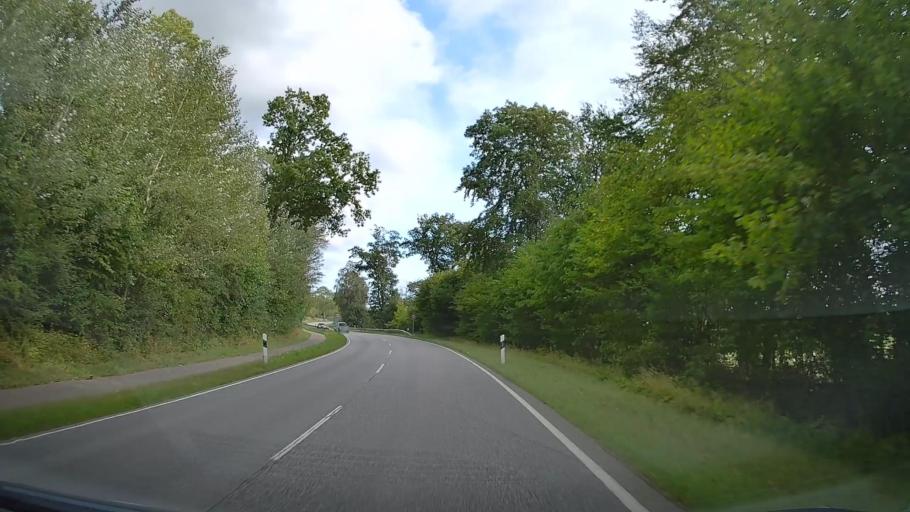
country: DE
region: Schleswig-Holstein
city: Niesgrau
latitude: 54.7502
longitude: 9.8506
